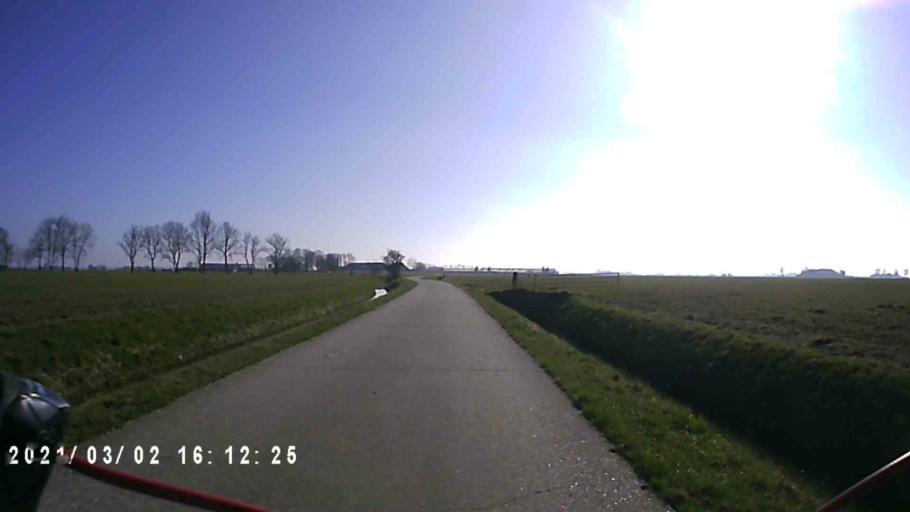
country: NL
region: Groningen
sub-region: Gemeente Zuidhorn
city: Oldehove
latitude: 53.2988
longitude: 6.3969
